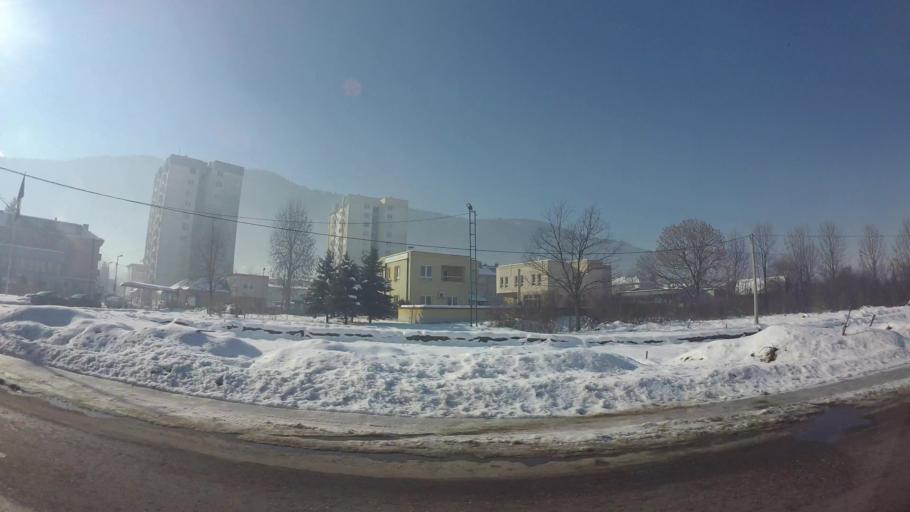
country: BA
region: Federation of Bosnia and Herzegovina
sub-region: Kanton Sarajevo
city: Sarajevo
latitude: 43.7996
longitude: 18.3131
